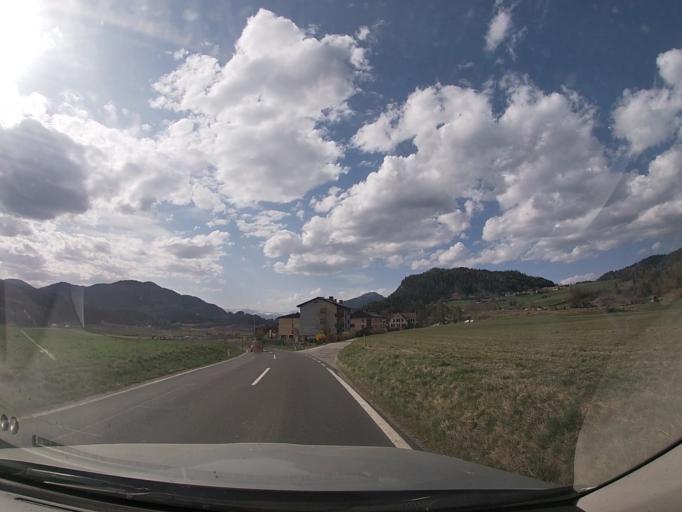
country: AT
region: Styria
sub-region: Politischer Bezirk Murau
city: Mariahof
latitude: 47.1014
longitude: 14.3855
